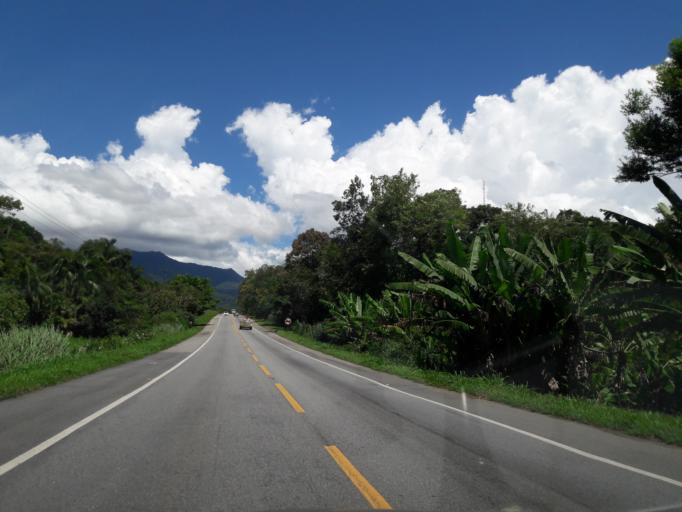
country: BR
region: Parana
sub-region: Antonina
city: Antonina
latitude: -25.5324
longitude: -48.7942
